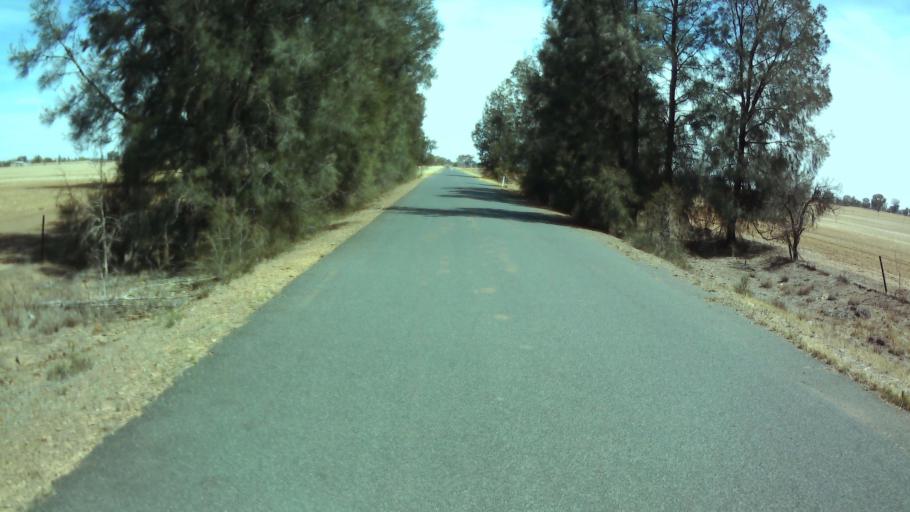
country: AU
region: New South Wales
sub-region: Weddin
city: Grenfell
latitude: -33.9295
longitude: 147.7626
